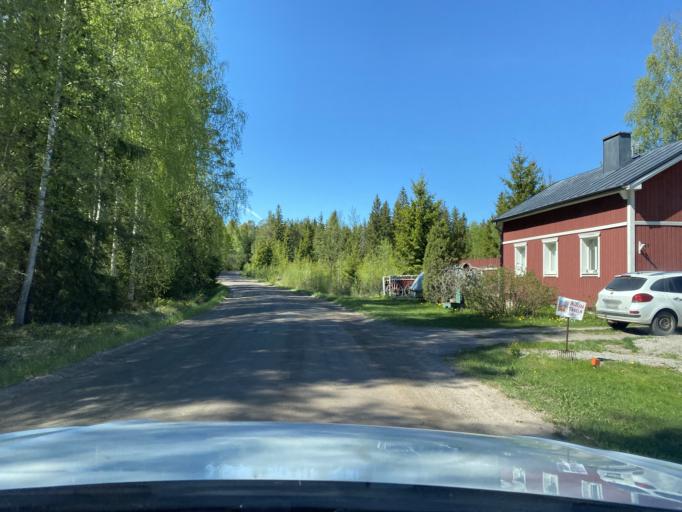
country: FI
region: Satakunta
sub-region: Rauma
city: Kiukainen
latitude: 61.1346
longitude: 21.9791
